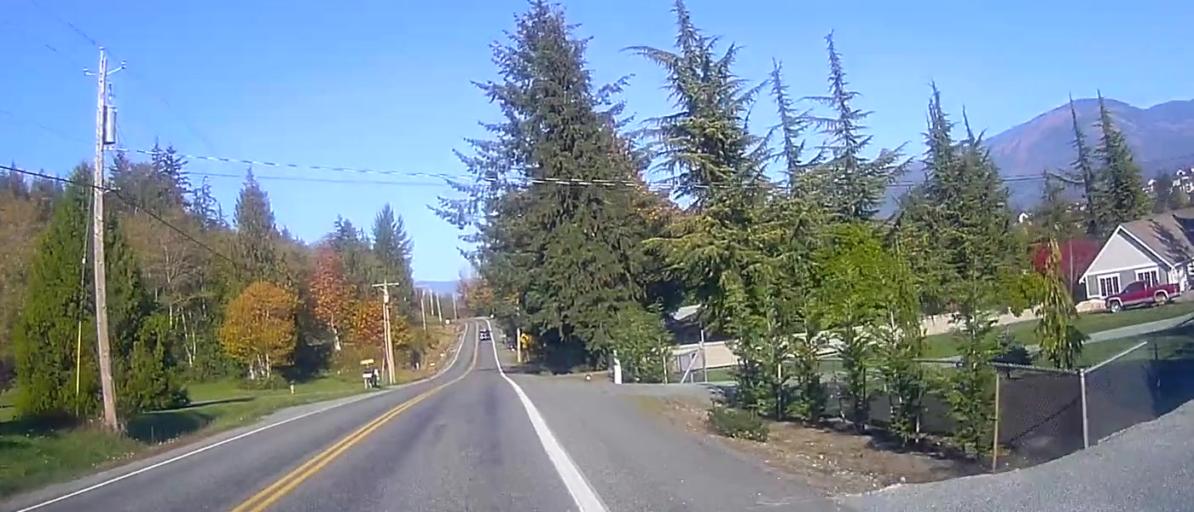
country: US
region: Washington
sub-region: Skagit County
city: Big Lake
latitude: 48.3960
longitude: -122.2448
